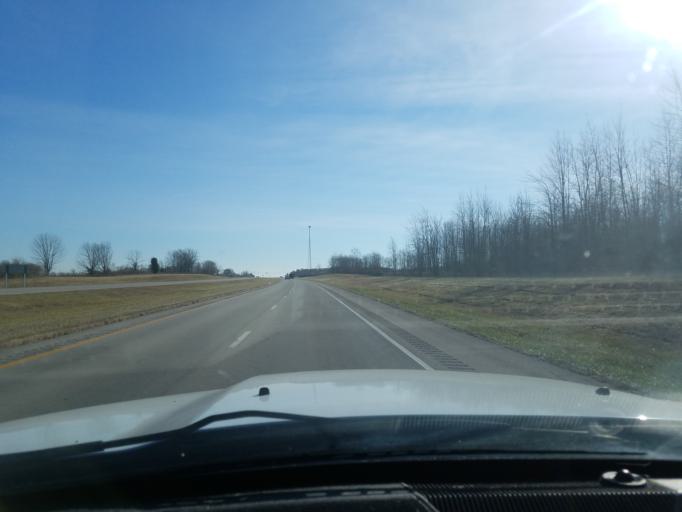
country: US
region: Ohio
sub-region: Adams County
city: Winchester
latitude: 38.9699
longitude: -83.7345
